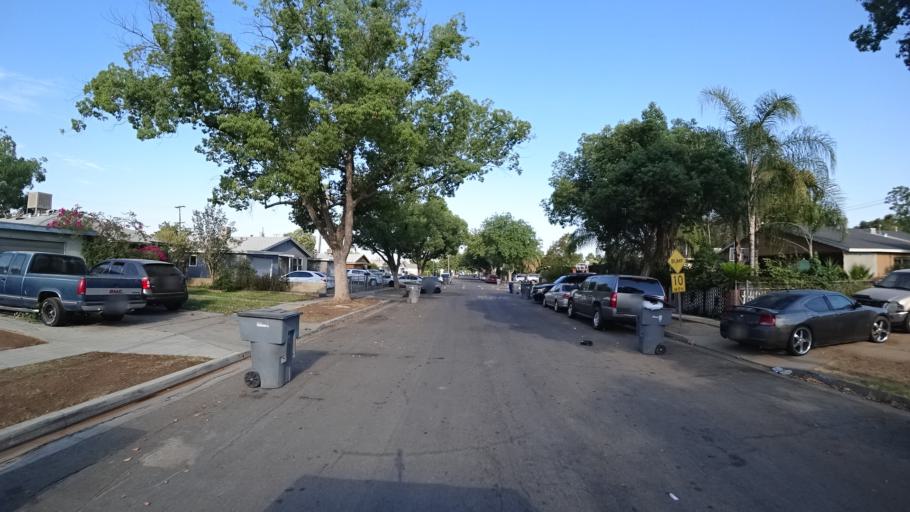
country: US
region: California
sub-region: Fresno County
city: West Park
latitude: 36.7243
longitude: -119.8139
